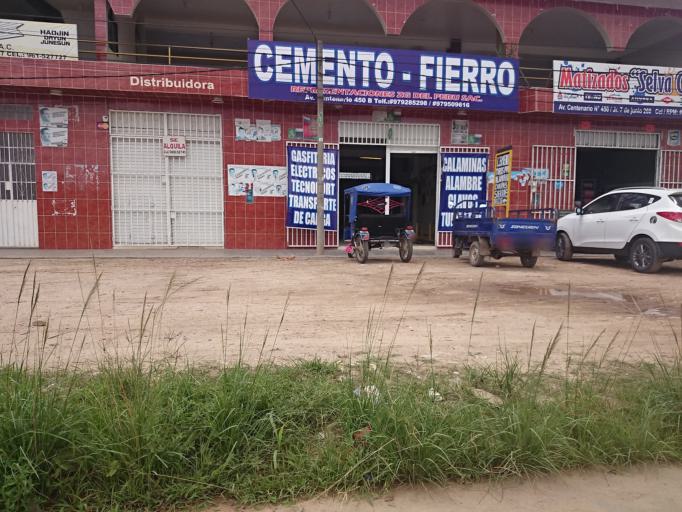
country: PE
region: Ucayali
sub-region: Provincia de Coronel Portillo
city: Pucallpa
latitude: -8.3833
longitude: -74.5437
